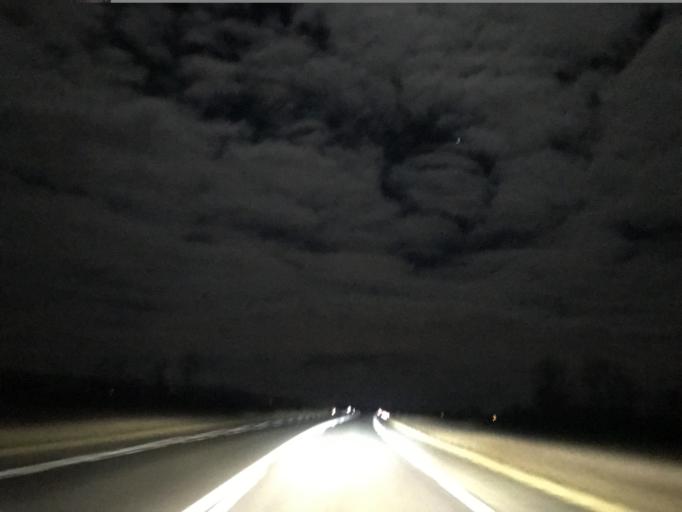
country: FR
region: Auvergne
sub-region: Departement de l'Allier
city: Hauterive
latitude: 46.0669
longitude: 3.4448
